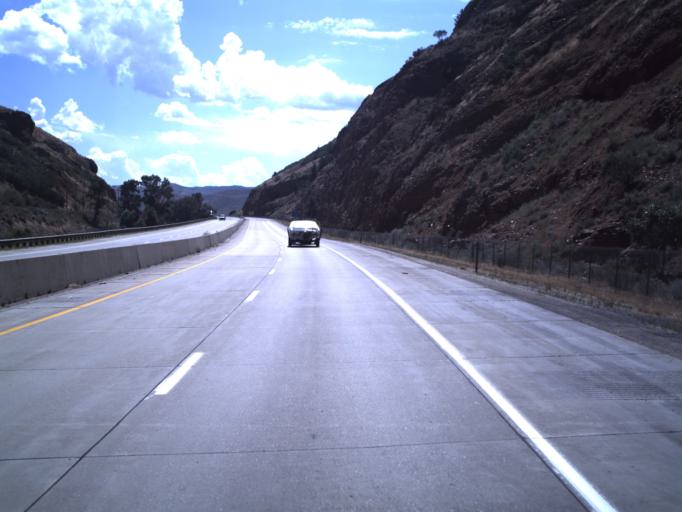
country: US
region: Utah
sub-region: Morgan County
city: Morgan
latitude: 41.0536
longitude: -111.5303
